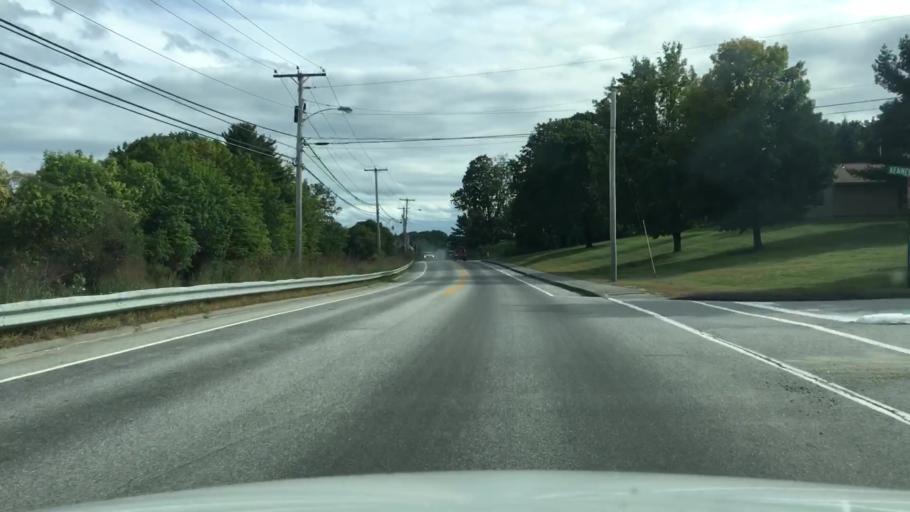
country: US
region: Maine
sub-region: Kennebec County
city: Farmingdale
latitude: 44.2510
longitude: -69.7722
